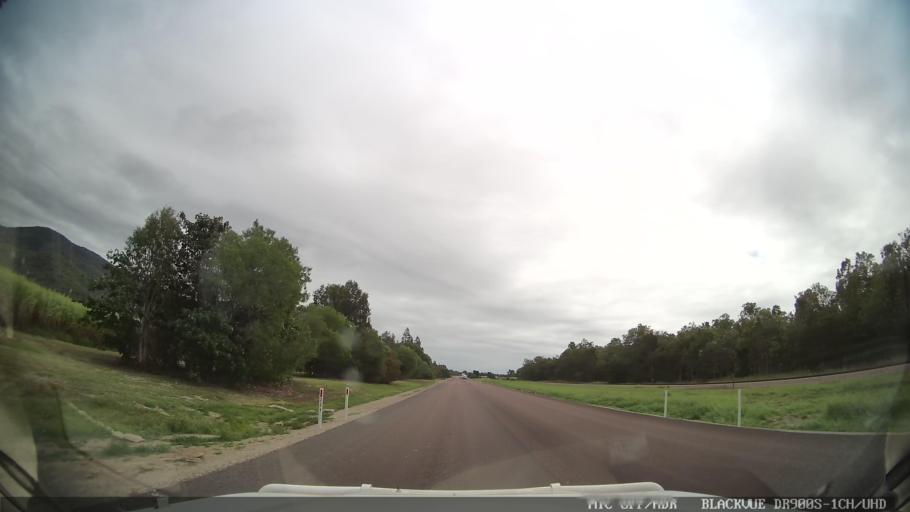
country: AU
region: Queensland
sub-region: Hinchinbrook
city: Ingham
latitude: -18.9271
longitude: 146.2639
